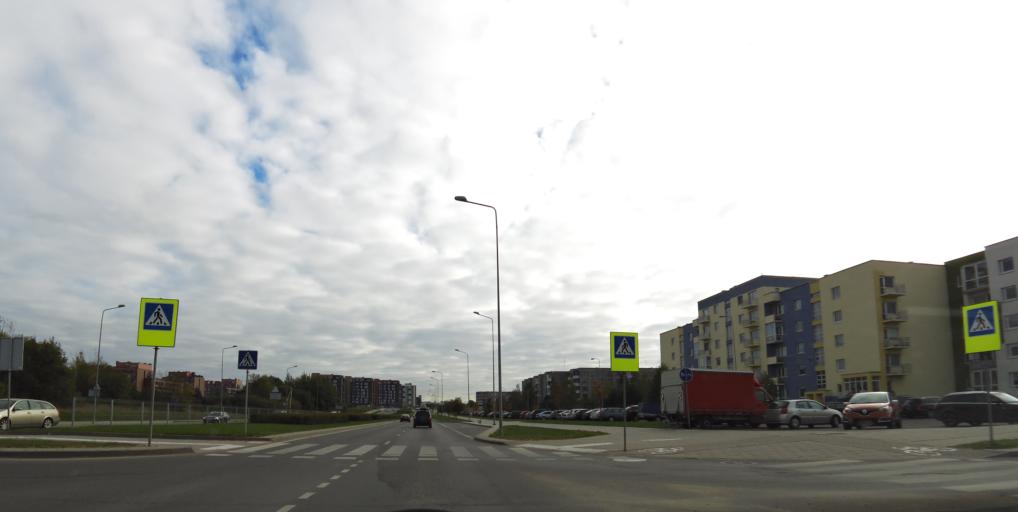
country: LT
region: Vilnius County
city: Pilaite
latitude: 54.7102
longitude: 25.1750
